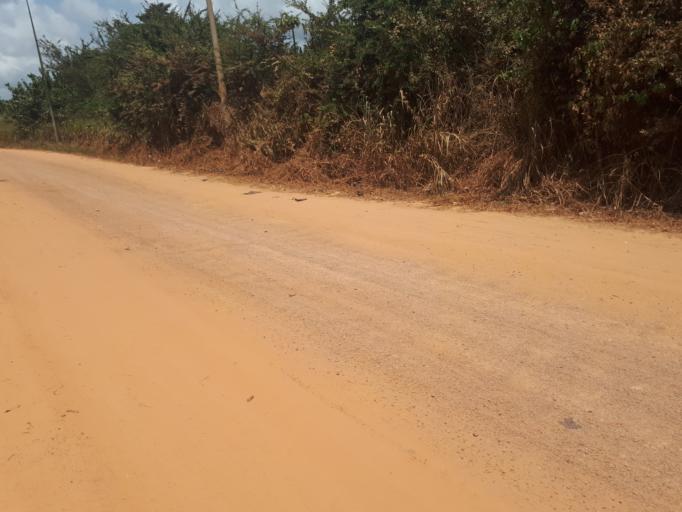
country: GH
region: Central
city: Cape Coast
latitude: 5.1227
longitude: -1.2926
